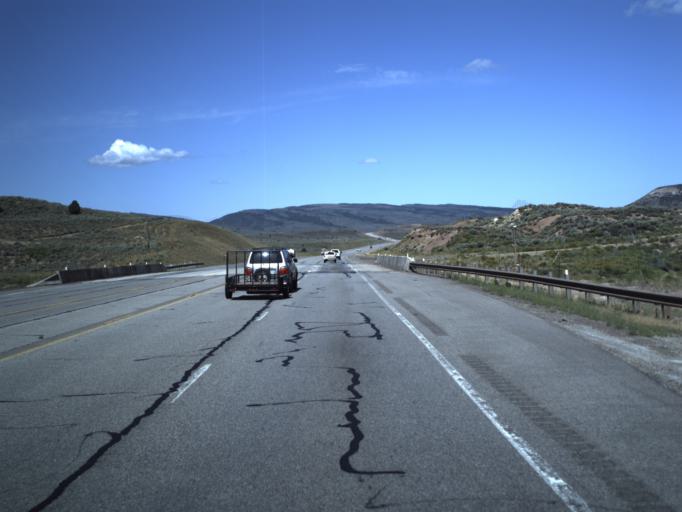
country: US
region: Utah
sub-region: Carbon County
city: Helper
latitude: 39.8313
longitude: -110.9648
